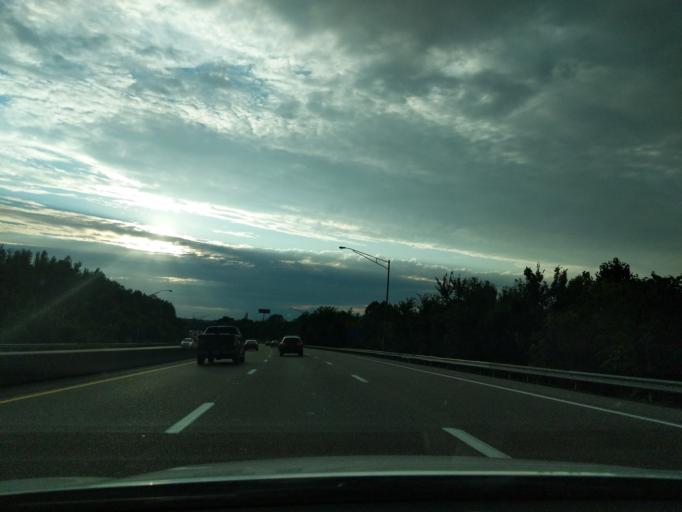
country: US
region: Tennessee
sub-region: Shelby County
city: New South Memphis
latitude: 35.0774
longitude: -90.0464
